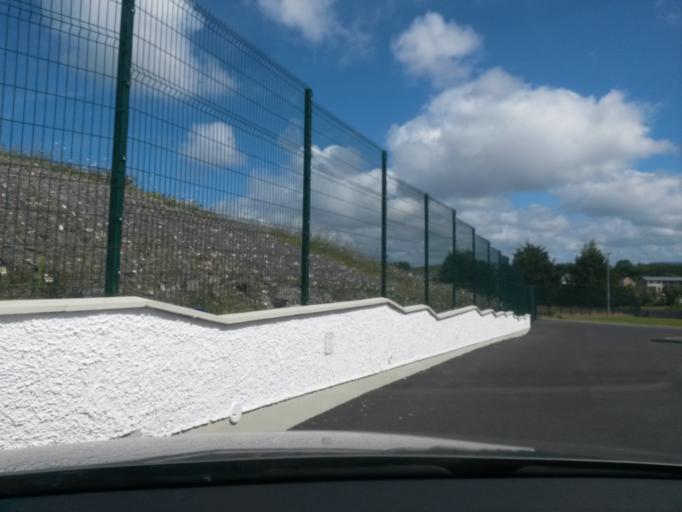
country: IE
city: Ballisodare
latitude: 54.2067
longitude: -8.5082
